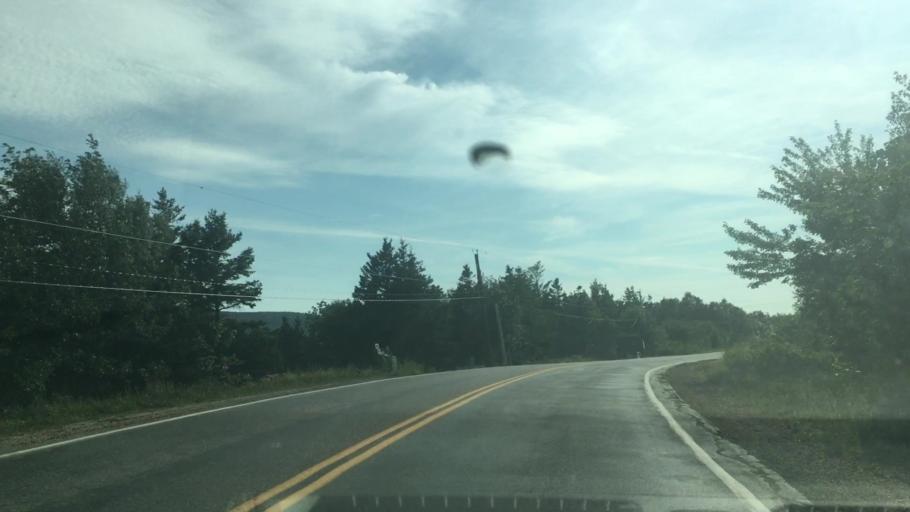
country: CA
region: Nova Scotia
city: Sydney Mines
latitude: 46.8784
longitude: -60.5172
